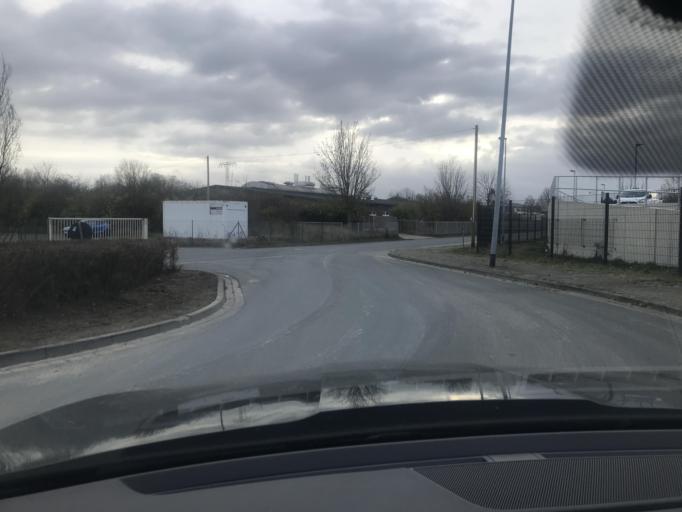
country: DE
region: Saxony-Anhalt
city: Quedlinburg
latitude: 51.7999
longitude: 11.1820
